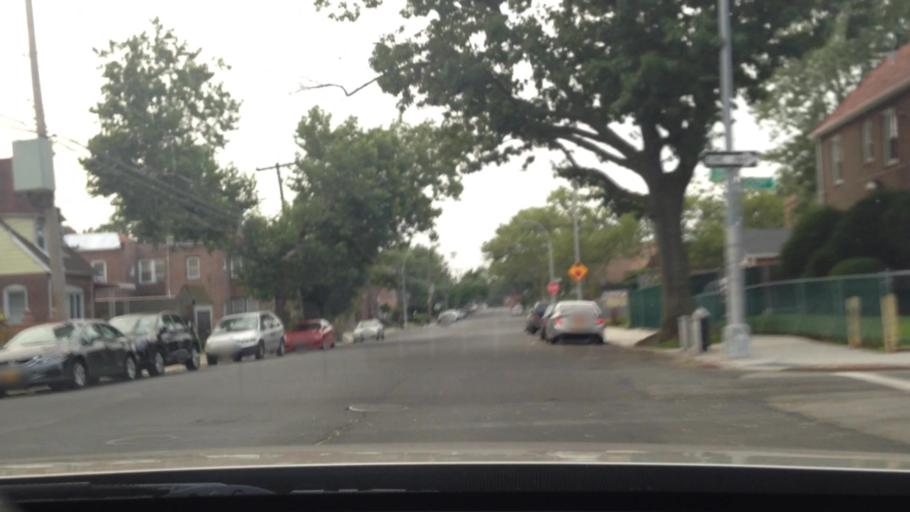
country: US
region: New York
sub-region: Nassau County
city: South Valley Stream
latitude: 40.6748
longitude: -73.7422
